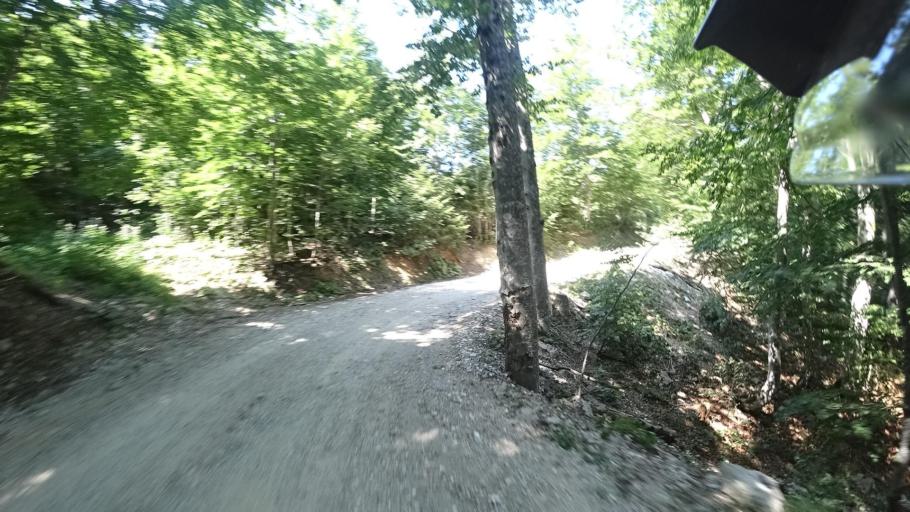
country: HR
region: Licko-Senjska
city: Popovaca
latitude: 44.5902
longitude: 15.1788
